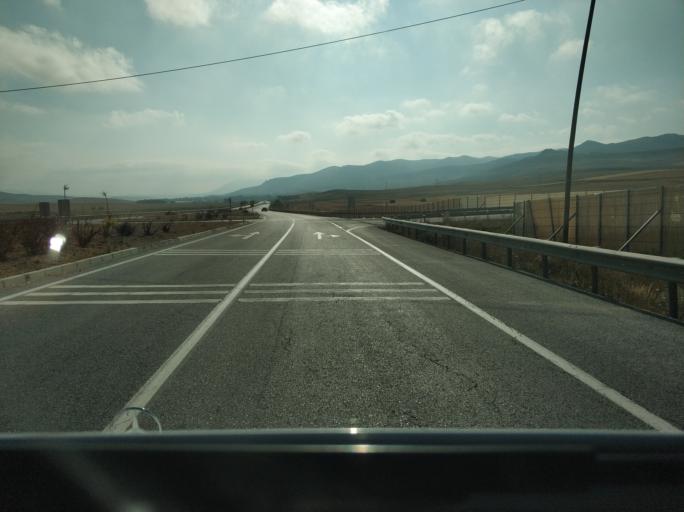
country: TR
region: Sivas
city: Yildizeli
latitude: 39.8350
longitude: 36.4266
